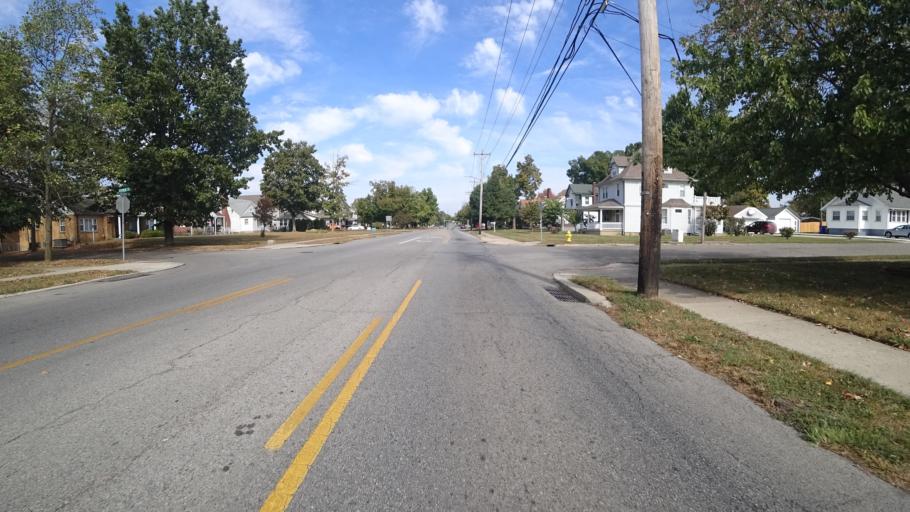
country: US
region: Ohio
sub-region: Butler County
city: Fairfield
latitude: 39.3639
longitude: -84.5579
